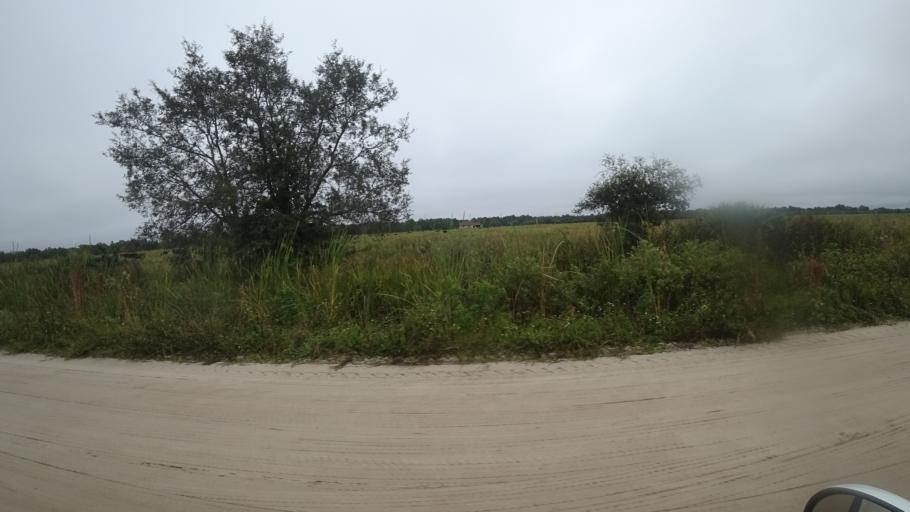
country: US
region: Florida
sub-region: Sarasota County
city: The Meadows
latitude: 27.4696
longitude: -82.3418
